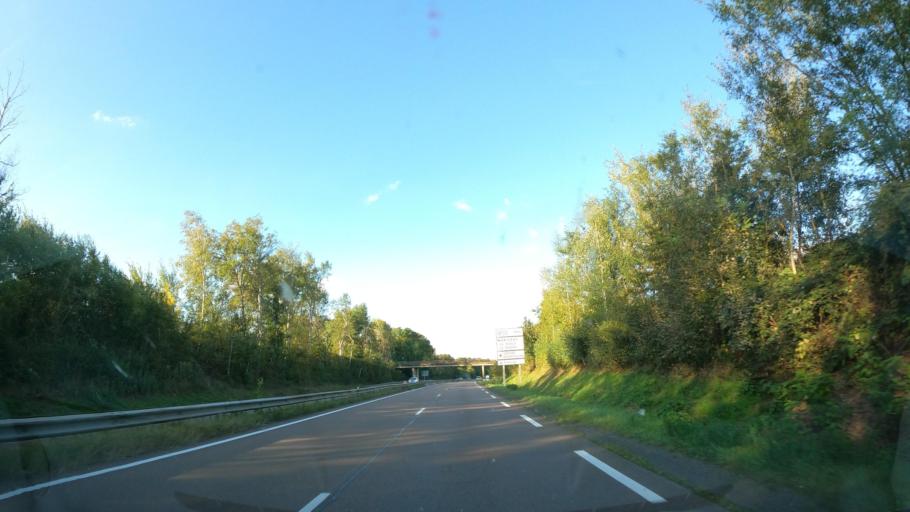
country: FR
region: Bourgogne
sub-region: Departement de Saone-et-Loire
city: Montceau-les-Mines
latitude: 46.6562
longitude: 4.3306
